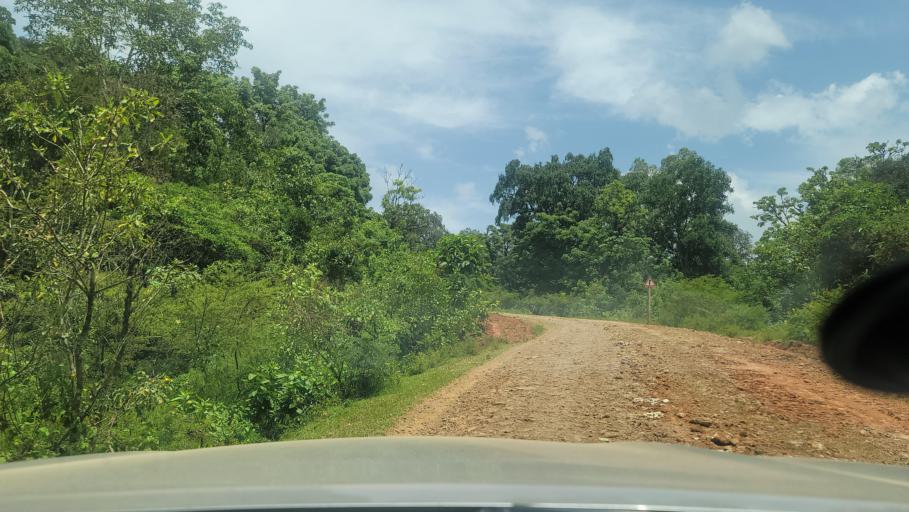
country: ET
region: Southern Nations, Nationalities, and People's Region
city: Bonga
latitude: 7.6865
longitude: 36.2421
